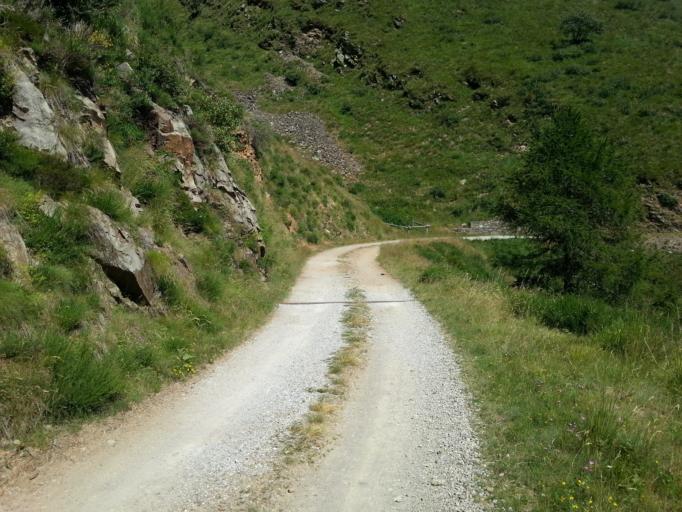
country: CH
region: Ticino
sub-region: Lugano District
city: Tesserete
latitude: 46.1041
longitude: 9.0101
